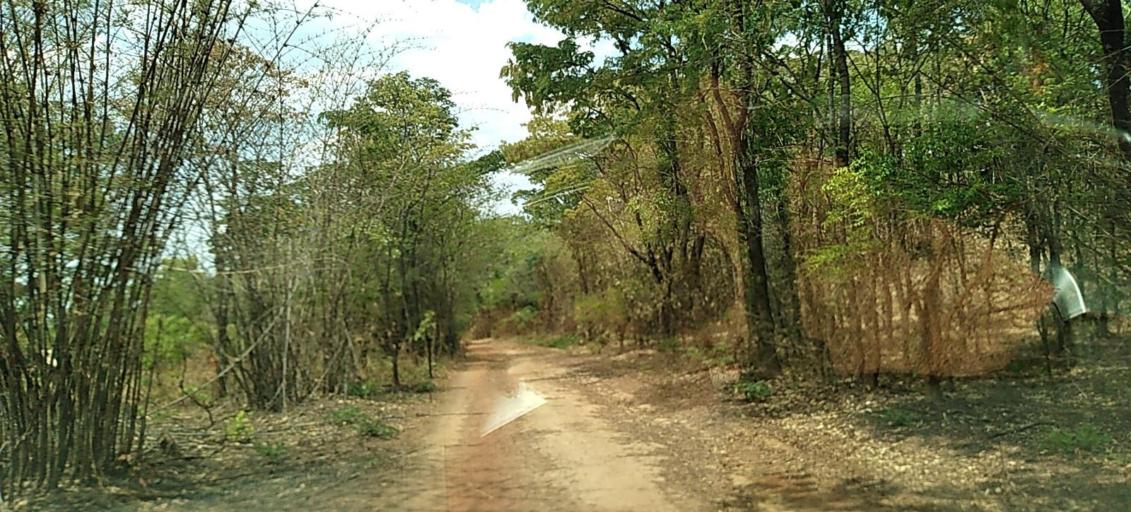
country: ZM
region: Copperbelt
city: Chililabombwe
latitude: -12.4771
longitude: 27.6471
